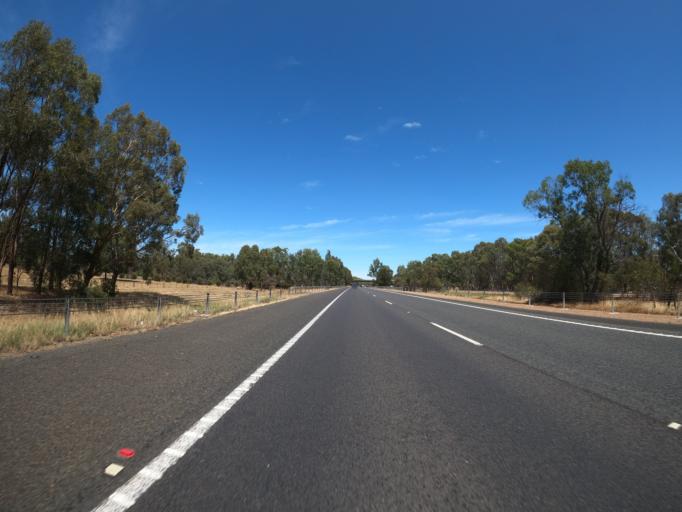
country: AU
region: Victoria
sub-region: Benalla
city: Benalla
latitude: -36.5723
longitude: 145.9951
